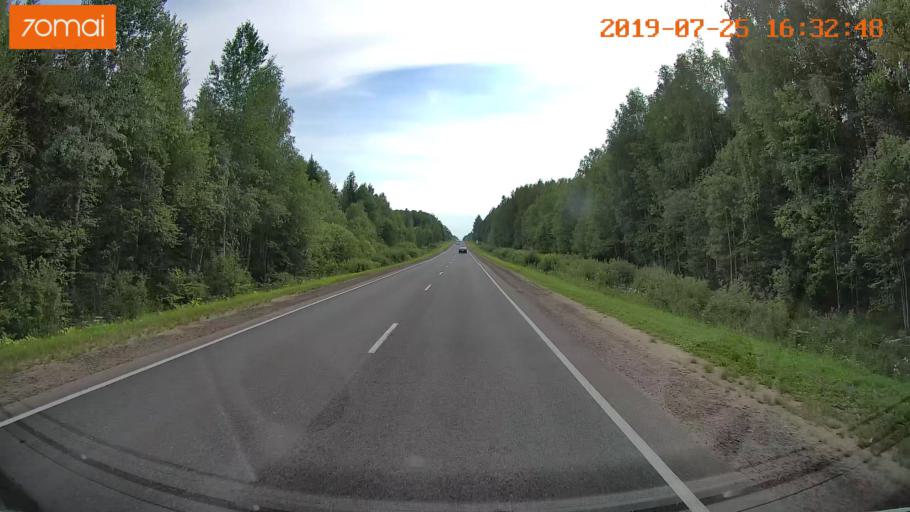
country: RU
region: Ivanovo
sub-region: Privolzhskiy Rayon
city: Ples
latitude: 57.4335
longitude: 41.4684
